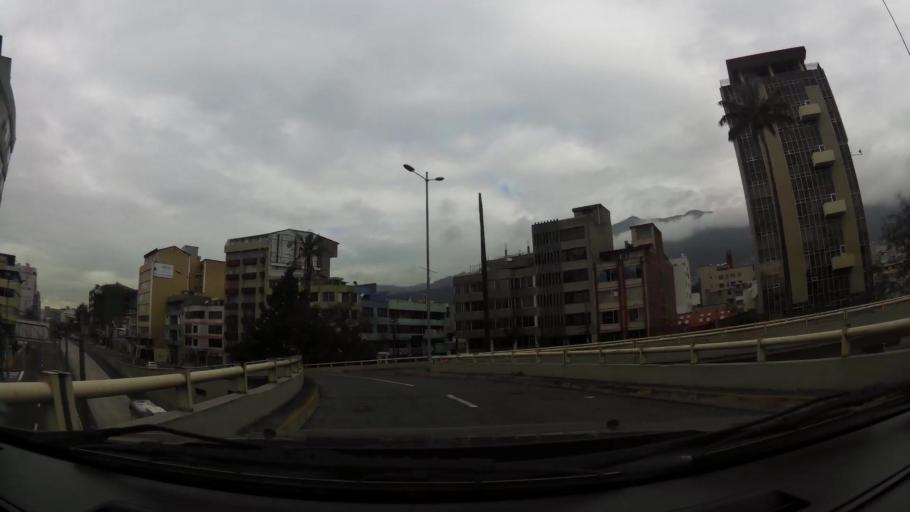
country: EC
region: Pichincha
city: Quito
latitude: -0.1960
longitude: -78.4950
